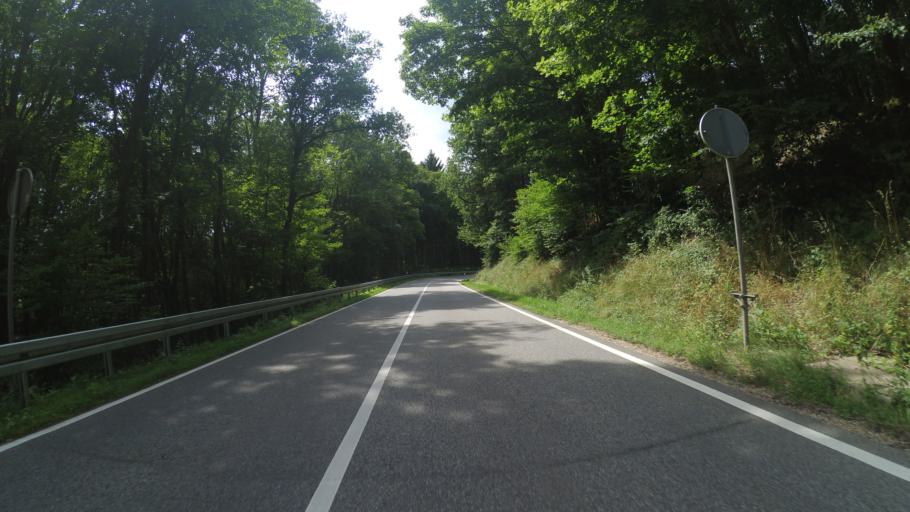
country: DE
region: Saarland
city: Tholey
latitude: 49.5283
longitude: 7.0063
